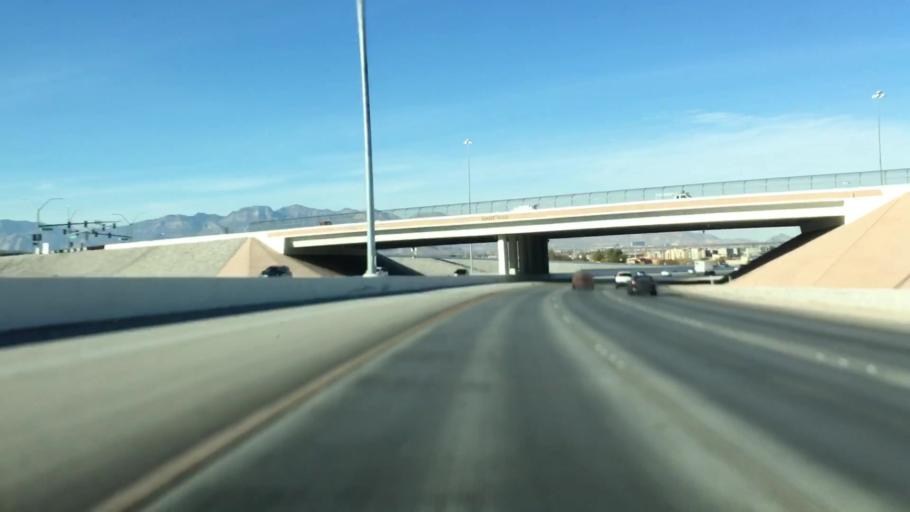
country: US
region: Nevada
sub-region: Clark County
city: Spring Valley
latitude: 36.0693
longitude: -115.2878
